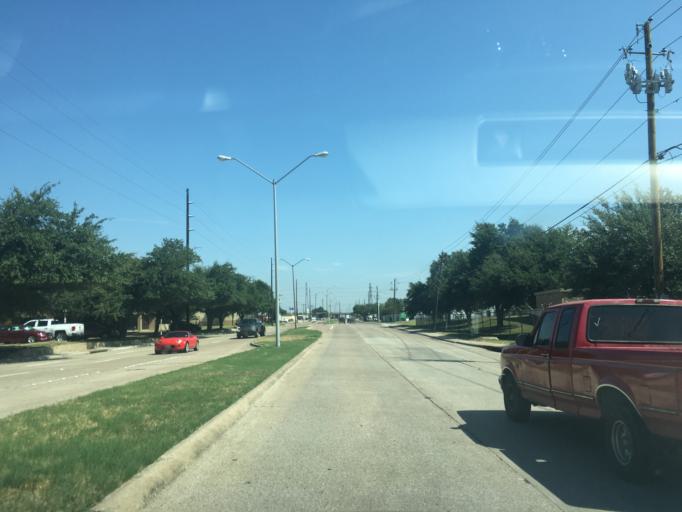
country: US
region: Texas
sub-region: Dallas County
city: Garland
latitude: 32.8596
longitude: -96.6657
